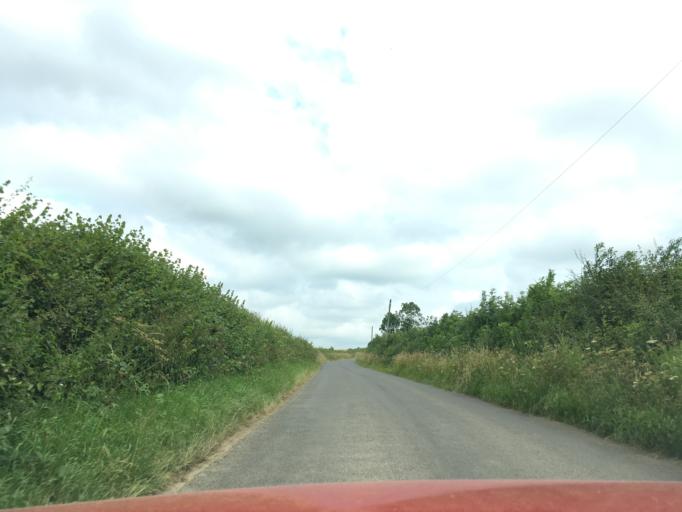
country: GB
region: England
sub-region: Oxfordshire
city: Bloxham
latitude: 51.9781
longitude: -1.3719
